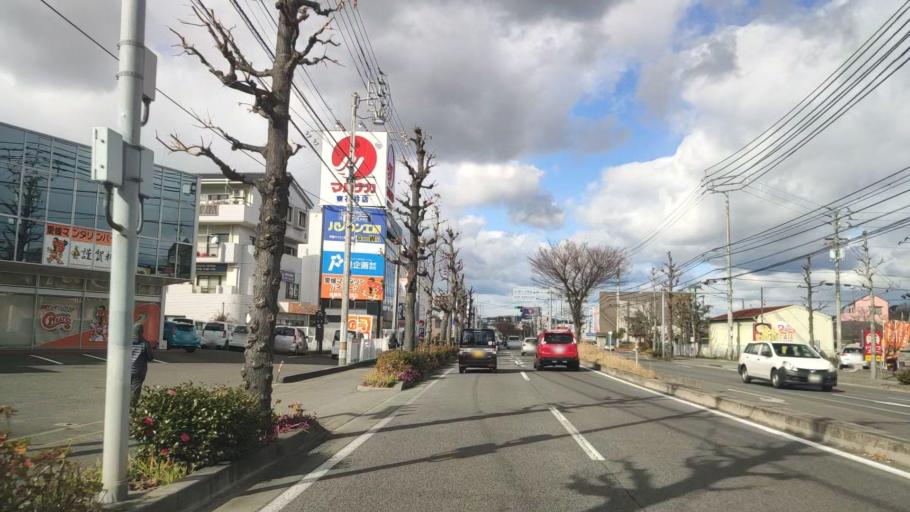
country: JP
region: Ehime
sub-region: Shikoku-chuo Shi
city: Matsuyama
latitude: 33.8124
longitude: 132.7786
